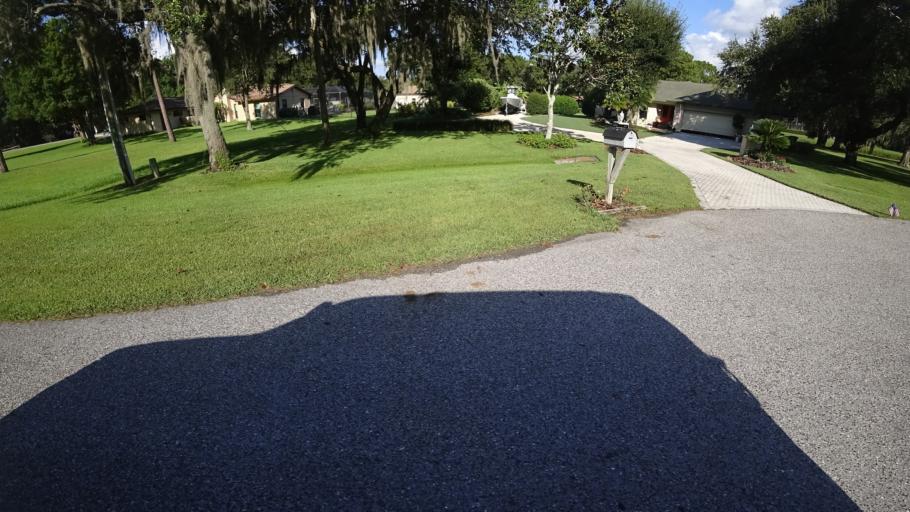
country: US
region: Florida
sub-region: Sarasota County
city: The Meadows
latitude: 27.4196
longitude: -82.4511
